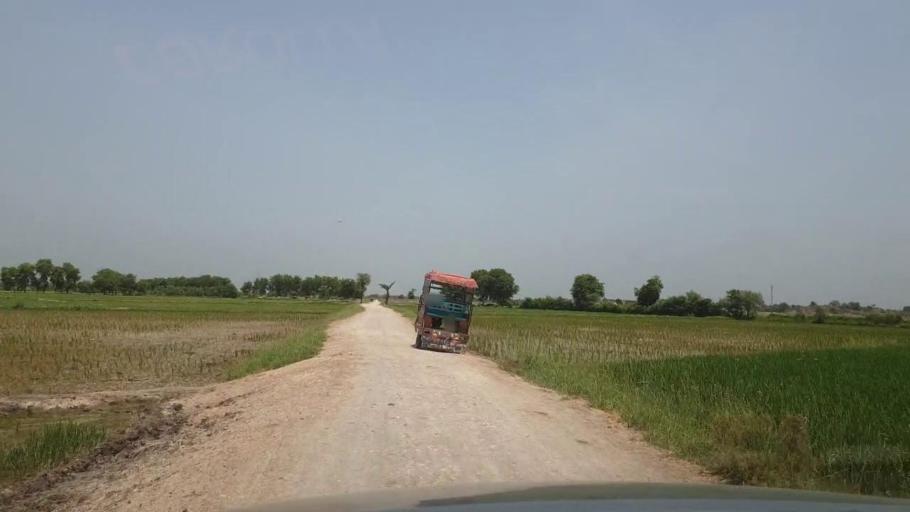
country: PK
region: Sindh
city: Madeji
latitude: 27.7574
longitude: 68.3736
